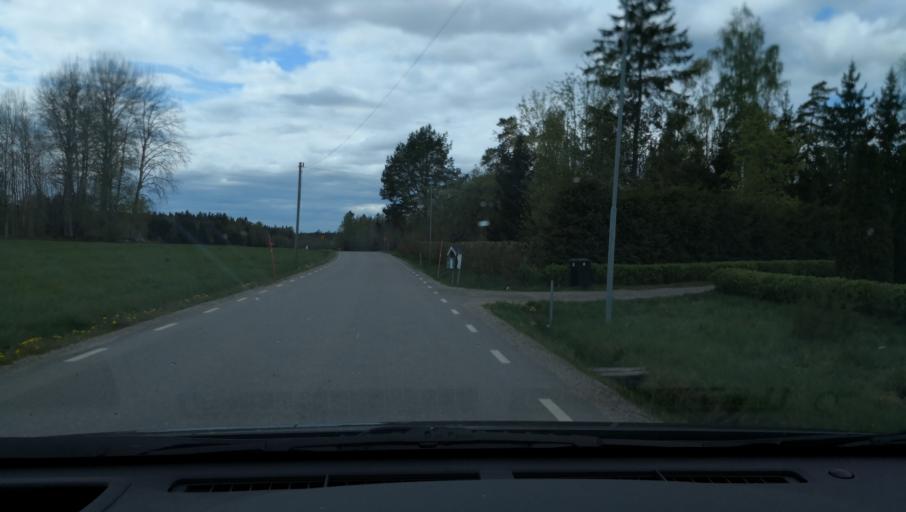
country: SE
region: Dalarna
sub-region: Avesta Kommun
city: Avesta
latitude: 60.0244
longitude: 16.2634
